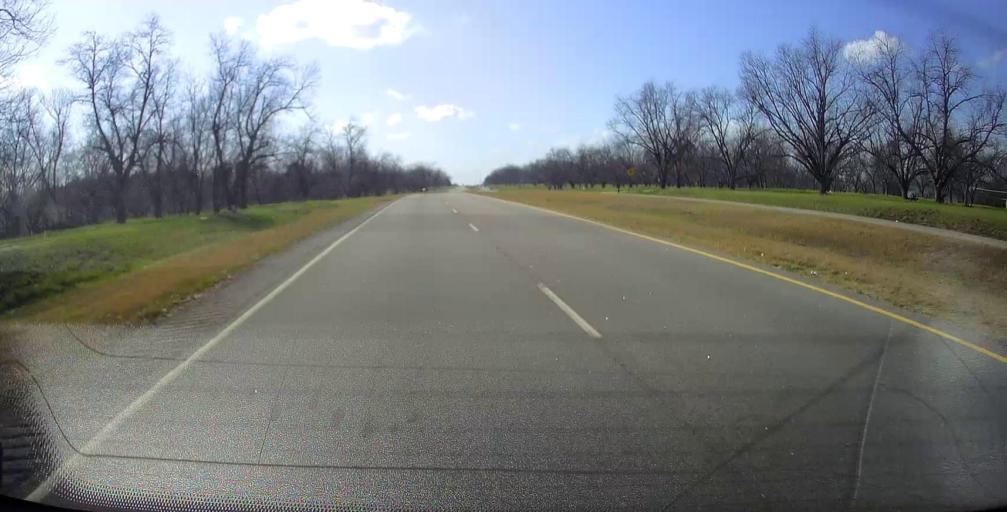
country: US
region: Georgia
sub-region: Dodge County
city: Eastman
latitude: 32.1981
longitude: -83.2229
